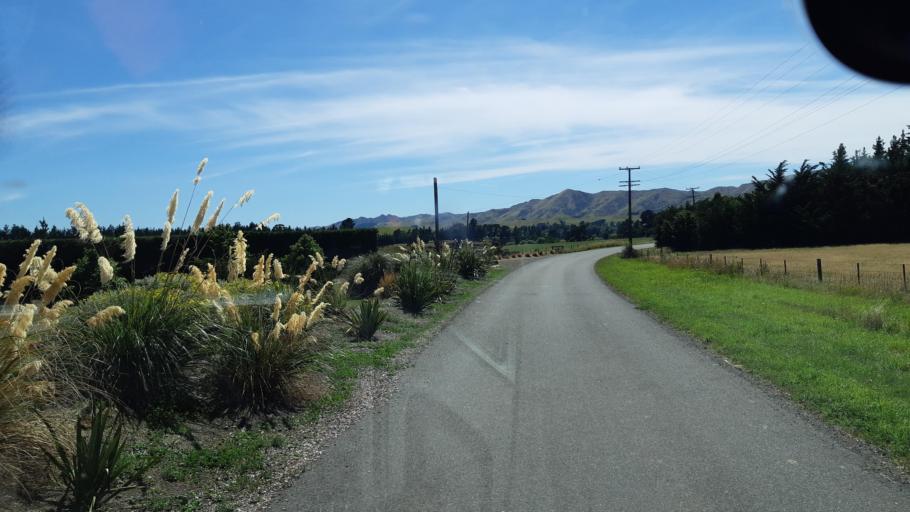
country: NZ
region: Marlborough
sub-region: Marlborough District
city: Blenheim
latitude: -41.8299
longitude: 174.1075
